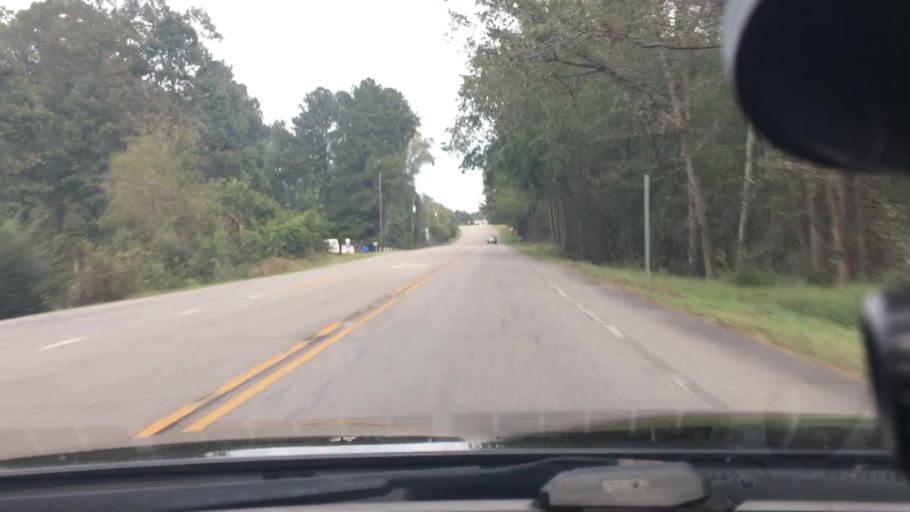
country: US
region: North Carolina
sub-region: Moore County
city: Carthage
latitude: 35.3487
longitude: -79.3643
